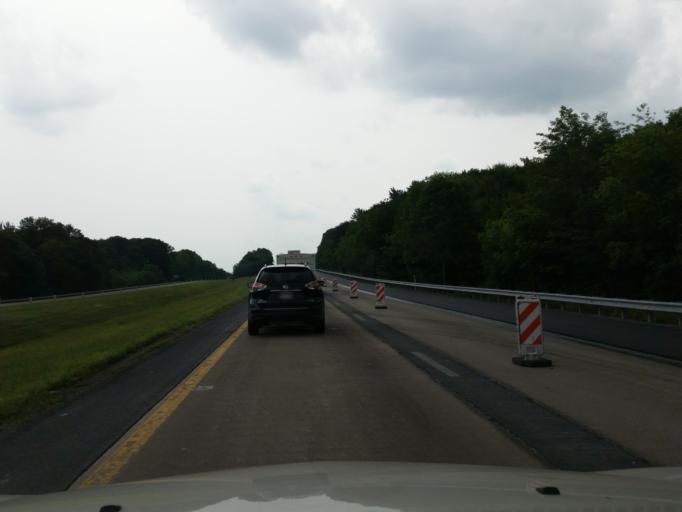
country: US
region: Pennsylvania
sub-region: Juniata County
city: Mifflintown
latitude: 40.5641
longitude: -77.2593
